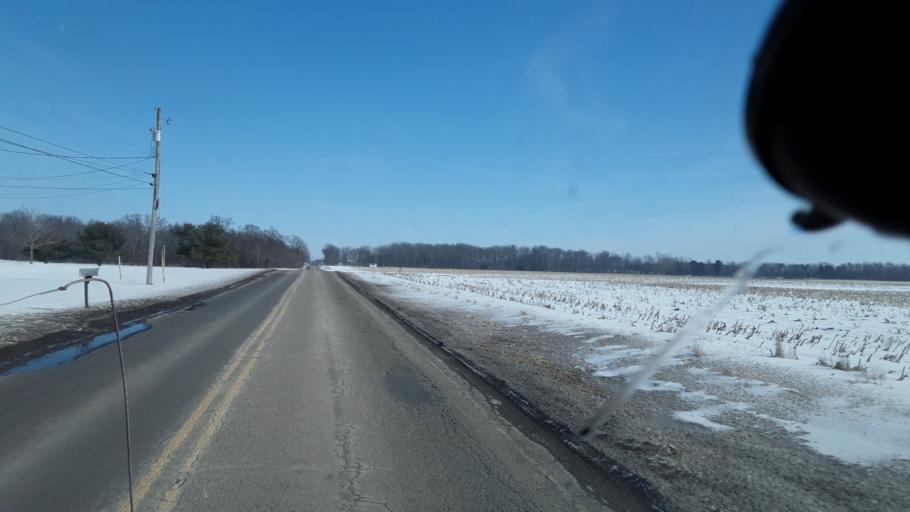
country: US
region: Ohio
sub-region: Mahoning County
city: Sebring
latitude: 40.9594
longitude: -81.0079
